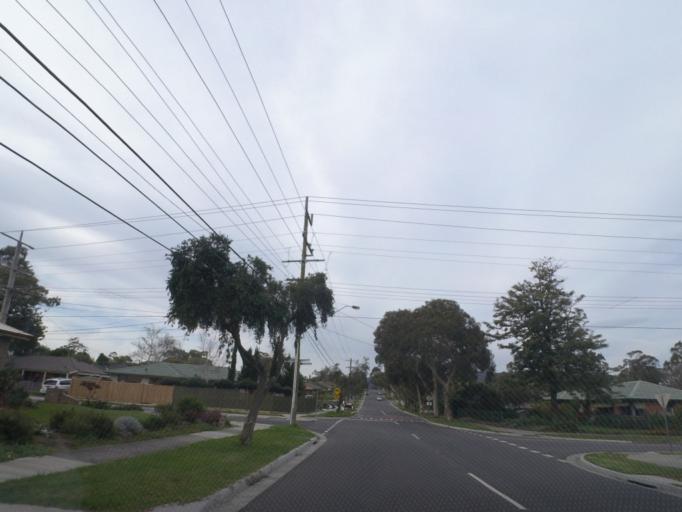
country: AU
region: Victoria
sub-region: Knox
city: Knoxfield
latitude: -37.8908
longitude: 145.2725
